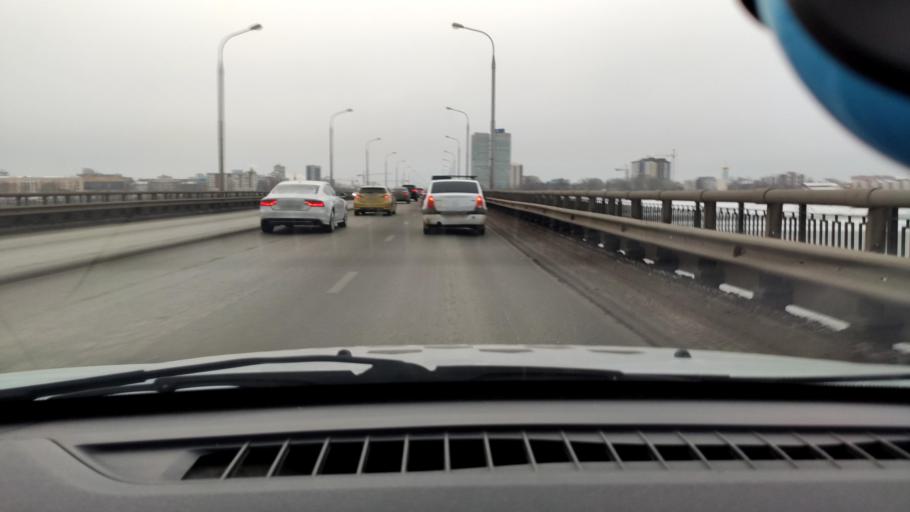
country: RU
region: Perm
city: Perm
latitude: 58.0230
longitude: 56.2206
